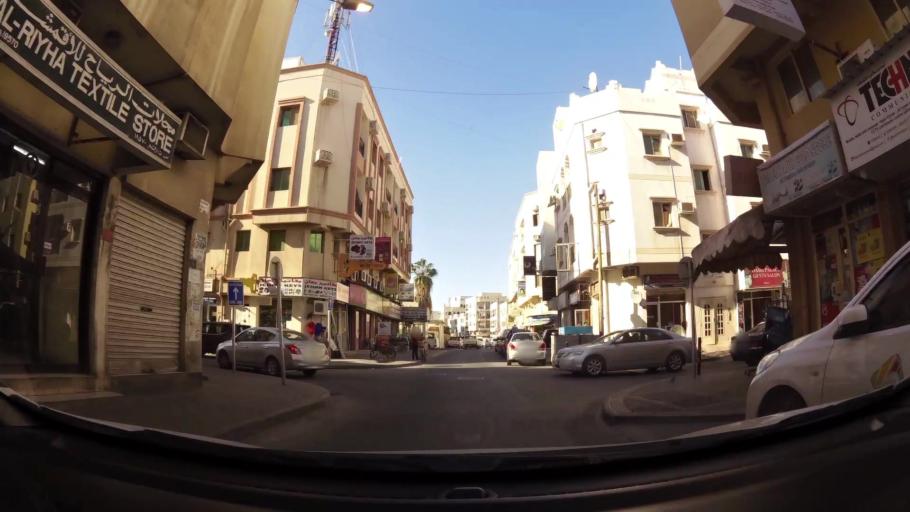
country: BH
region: Manama
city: Manama
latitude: 26.2325
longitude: 50.5874
